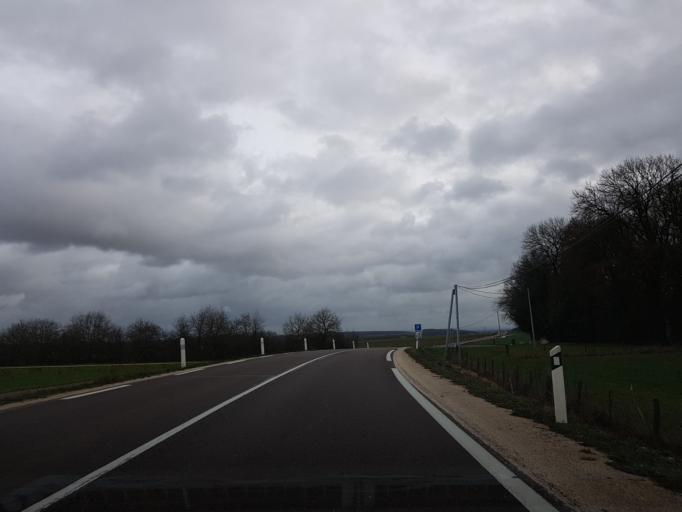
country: FR
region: Champagne-Ardenne
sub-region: Departement de la Haute-Marne
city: Fayl-Billot
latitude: 47.7688
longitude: 5.7059
